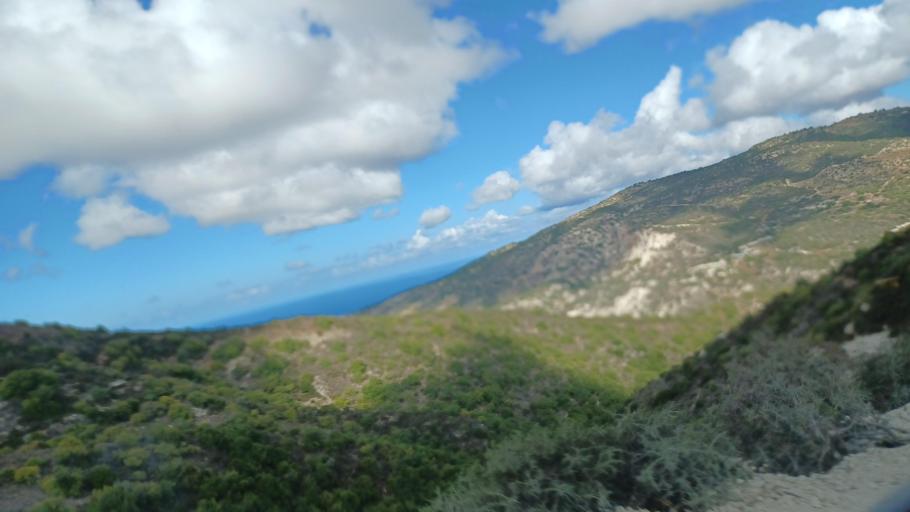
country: CY
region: Pafos
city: Tala
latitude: 34.8673
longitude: 32.4471
